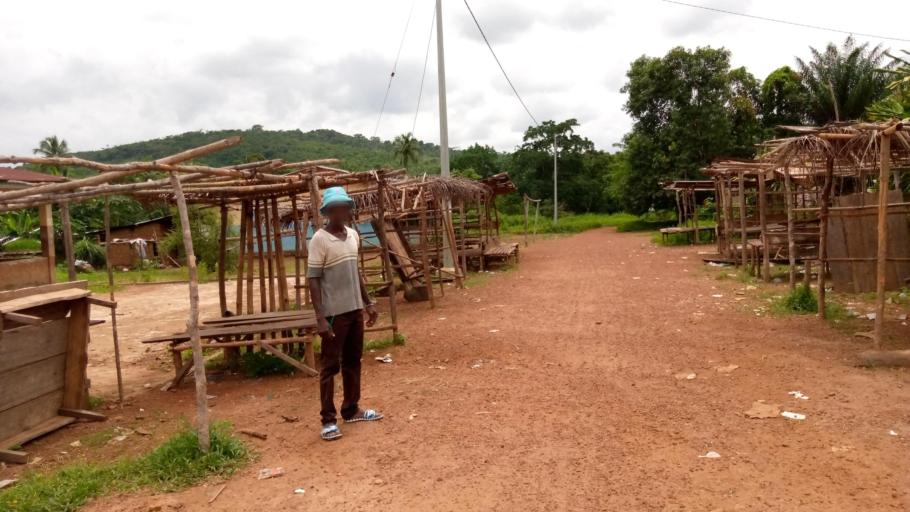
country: SL
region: Southern Province
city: Rotifunk
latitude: 8.1889
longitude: -12.5743
